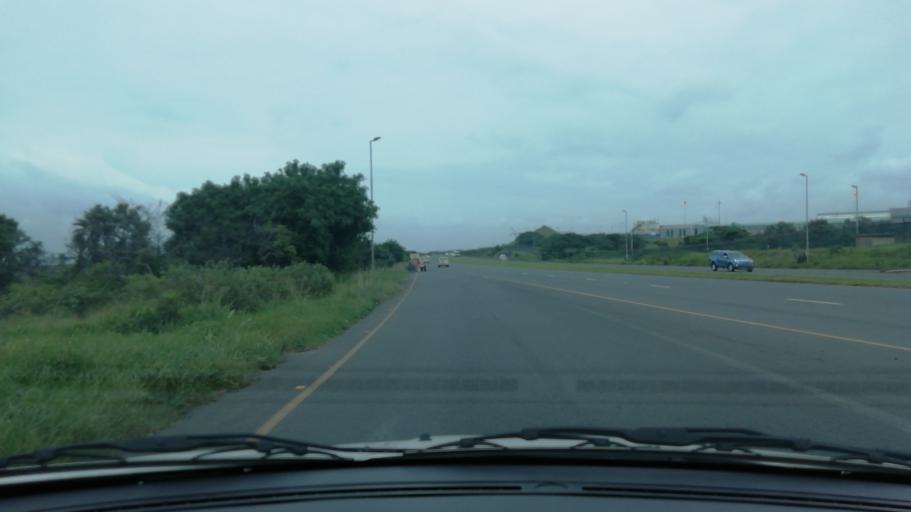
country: ZA
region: KwaZulu-Natal
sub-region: uThungulu District Municipality
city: Richards Bay
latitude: -28.7711
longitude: 32.0323
